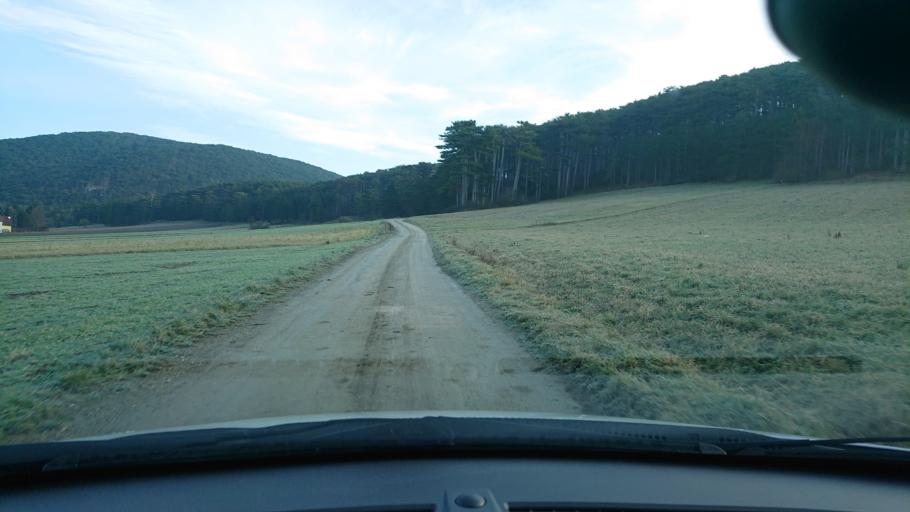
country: AT
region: Lower Austria
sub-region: Politischer Bezirk Baden
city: Berndorf
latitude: 47.9286
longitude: 16.0976
